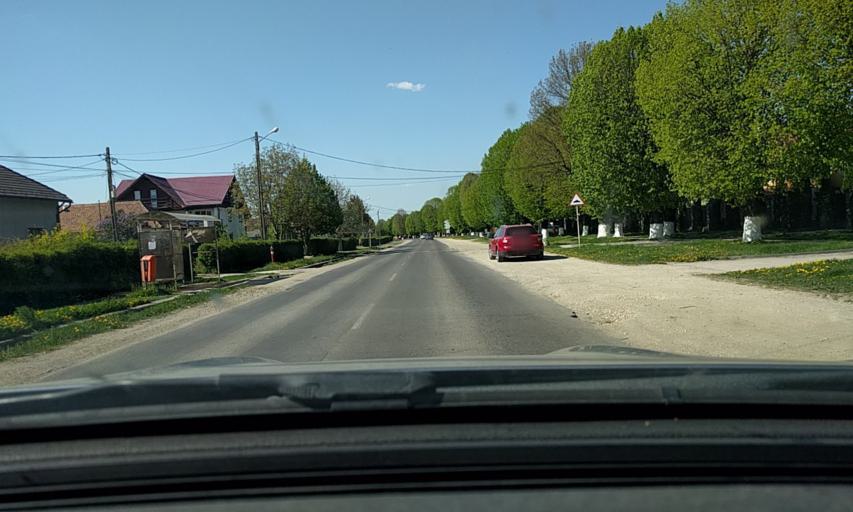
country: RO
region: Brasov
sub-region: Comuna Harman
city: Harman
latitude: 45.7060
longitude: 25.6877
